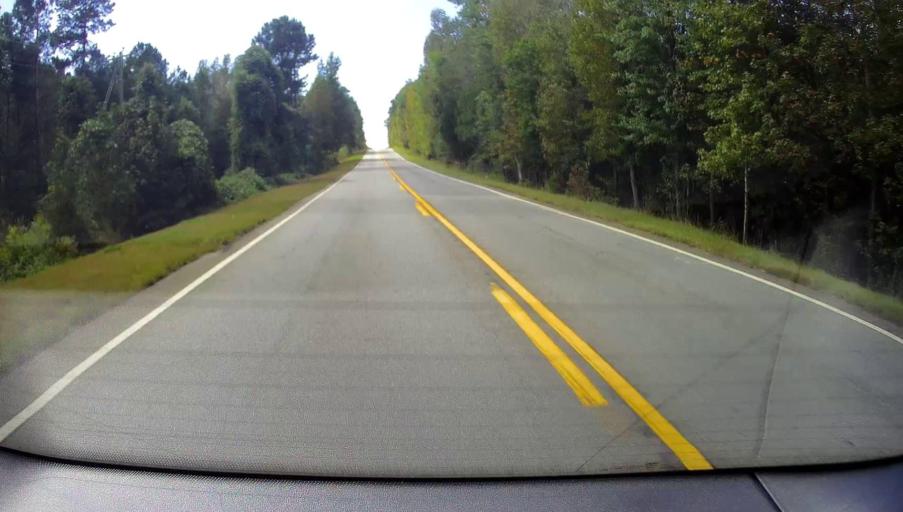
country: US
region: Georgia
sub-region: Jones County
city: Gray
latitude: 32.9605
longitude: -83.4381
